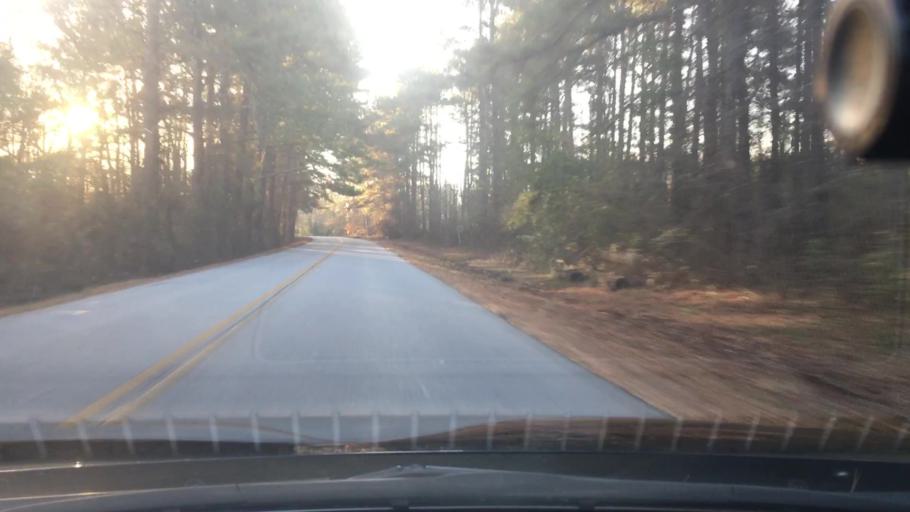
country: US
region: Georgia
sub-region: Coweta County
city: Senoia
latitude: 33.3160
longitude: -84.4787
